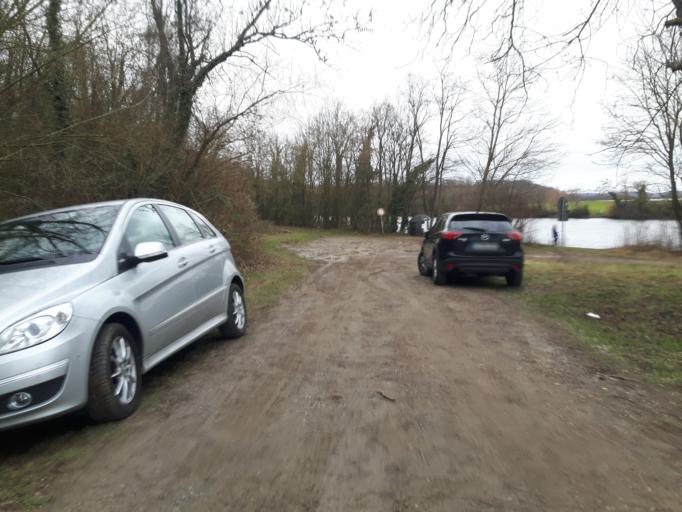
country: DE
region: Baden-Wuerttemberg
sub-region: Regierungsbezirk Stuttgart
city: Neckarwestheim
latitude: 49.0476
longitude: 9.1745
